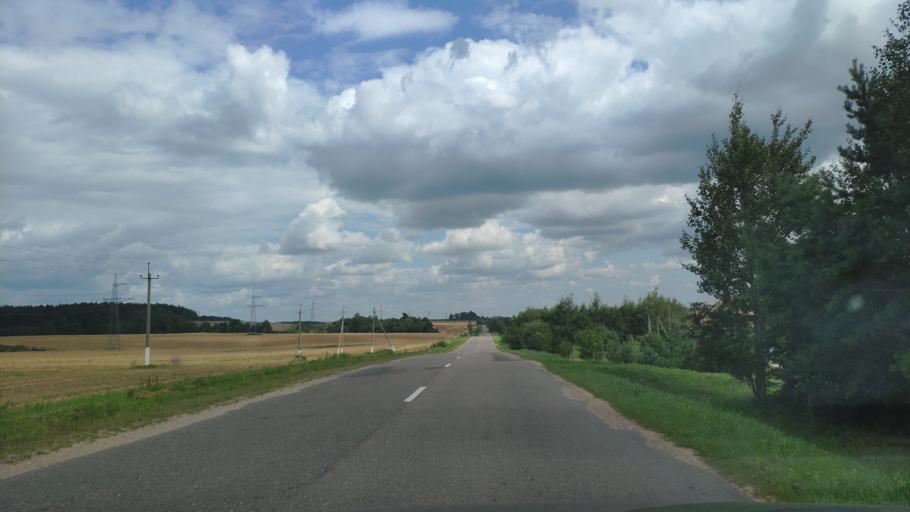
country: BY
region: Minsk
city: Khatsyezhyna
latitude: 53.8734
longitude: 27.3009
